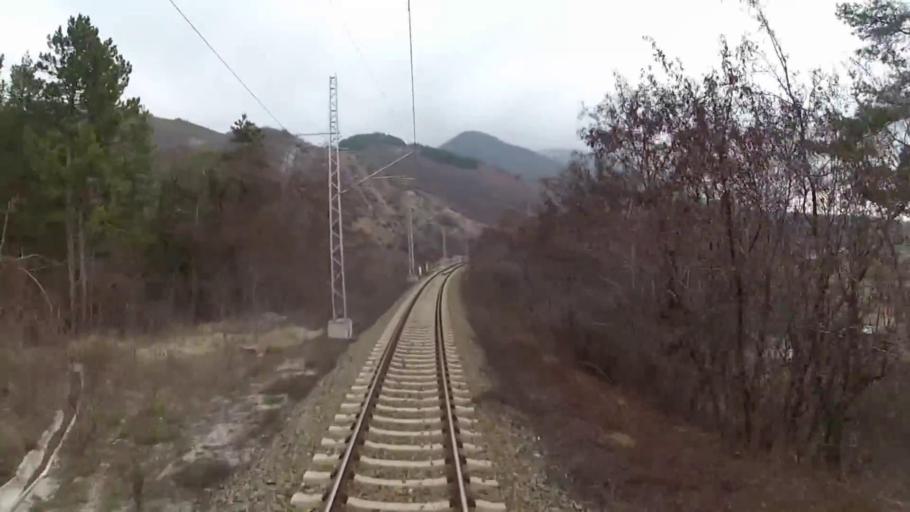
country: BG
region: Sofiya
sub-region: Obshtina Mirkovo
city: Mirkovo
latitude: 42.7196
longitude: 23.9294
